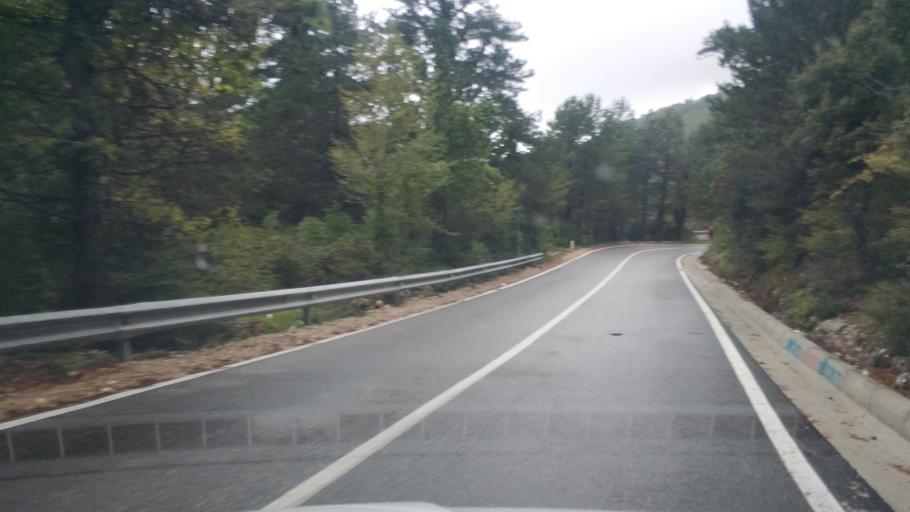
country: AL
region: Vlore
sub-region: Rrethi i Vlores
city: Brataj
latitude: 40.2047
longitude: 19.5863
